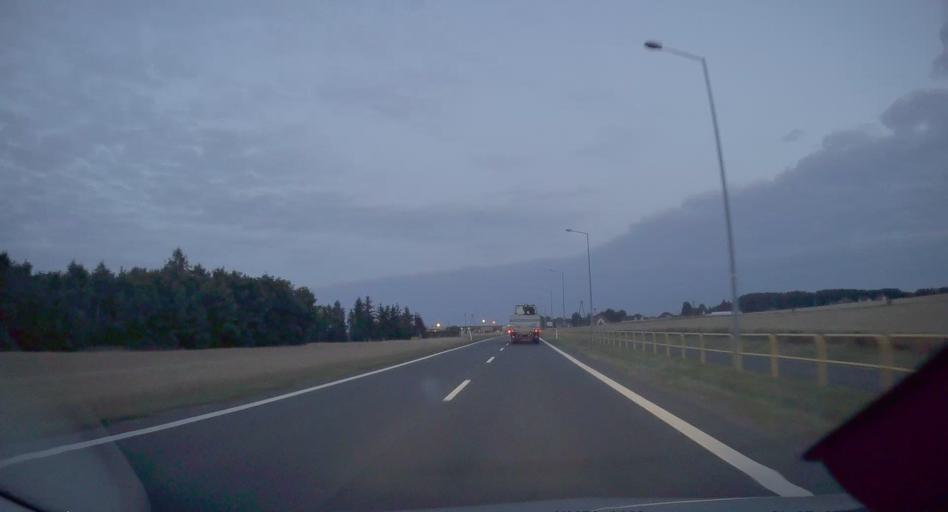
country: PL
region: Silesian Voivodeship
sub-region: Powiat klobucki
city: Opatow
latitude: 50.9324
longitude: 18.8553
